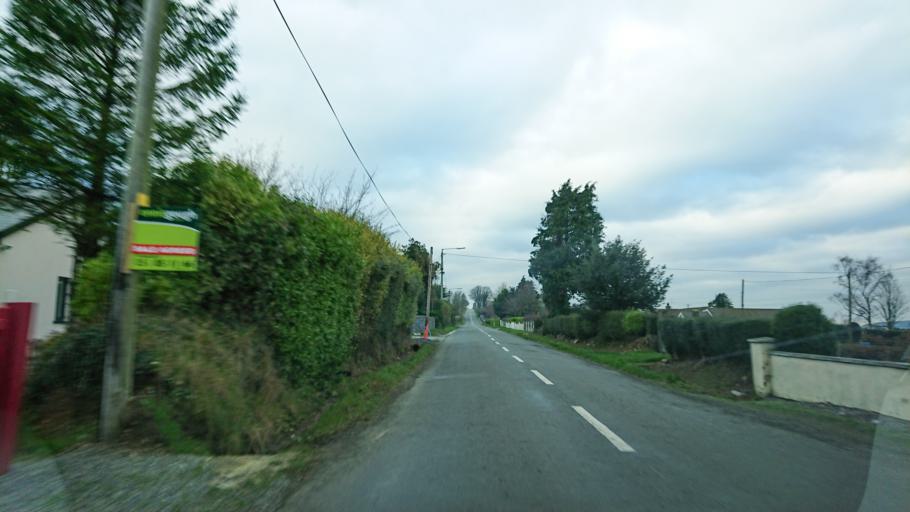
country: IE
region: Munster
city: Carrick-on-Suir
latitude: 52.3105
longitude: -7.5158
